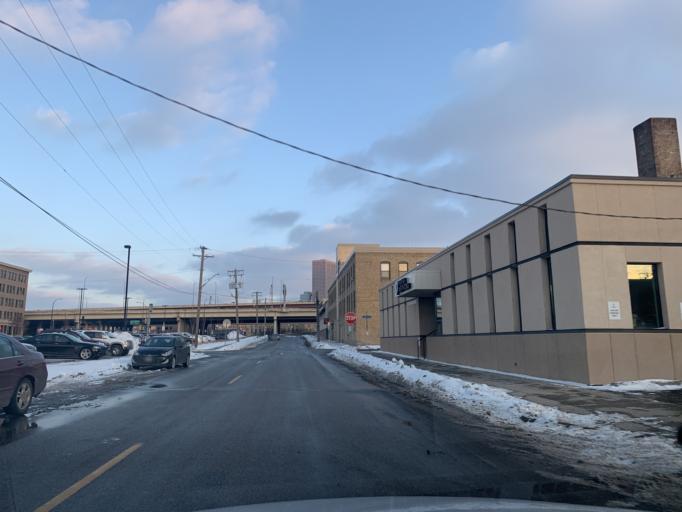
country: US
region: Minnesota
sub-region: Hennepin County
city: Minneapolis
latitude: 44.9789
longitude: -93.2902
